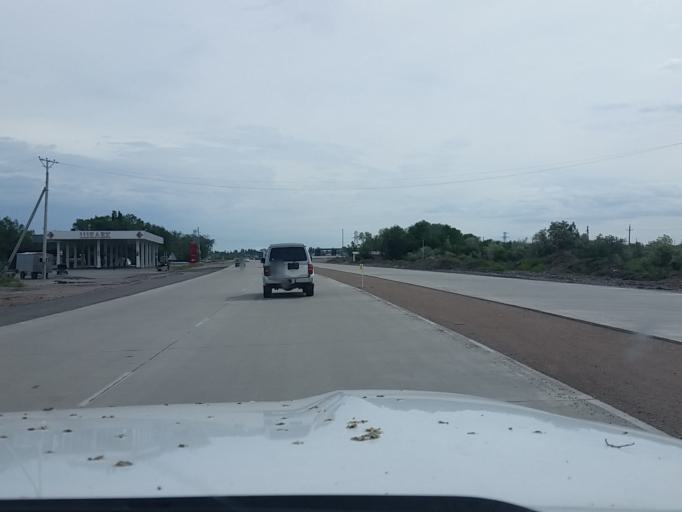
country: KZ
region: Almaty Oblysy
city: Turgen'
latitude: 43.5797
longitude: 78.2101
